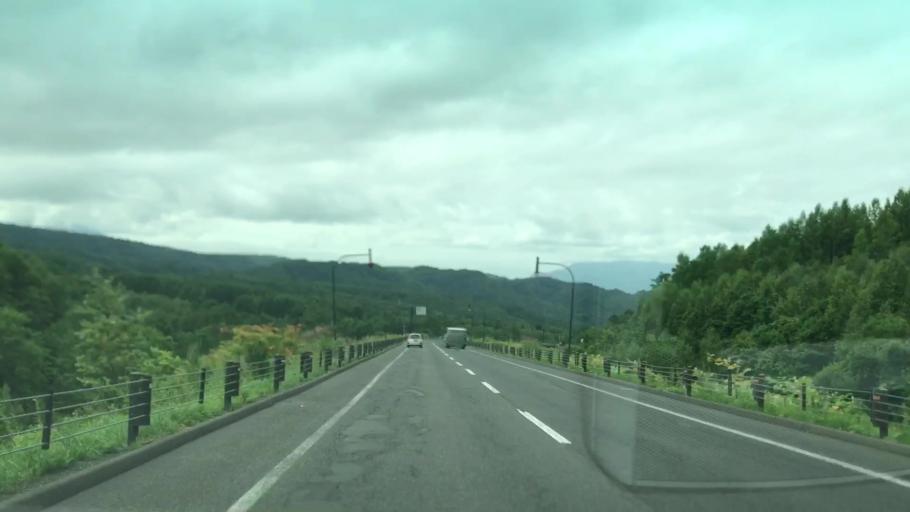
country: JP
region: Hokkaido
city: Niseko Town
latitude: 42.9544
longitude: 140.8635
